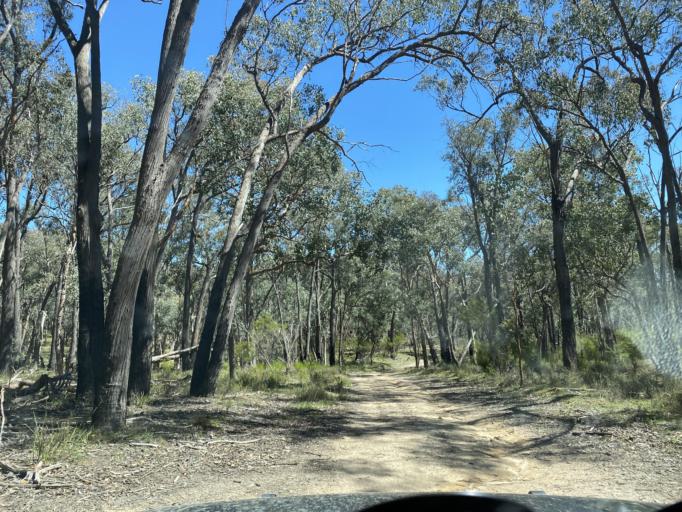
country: AU
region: Victoria
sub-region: Benalla
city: Benalla
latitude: -36.7043
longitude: 146.1541
